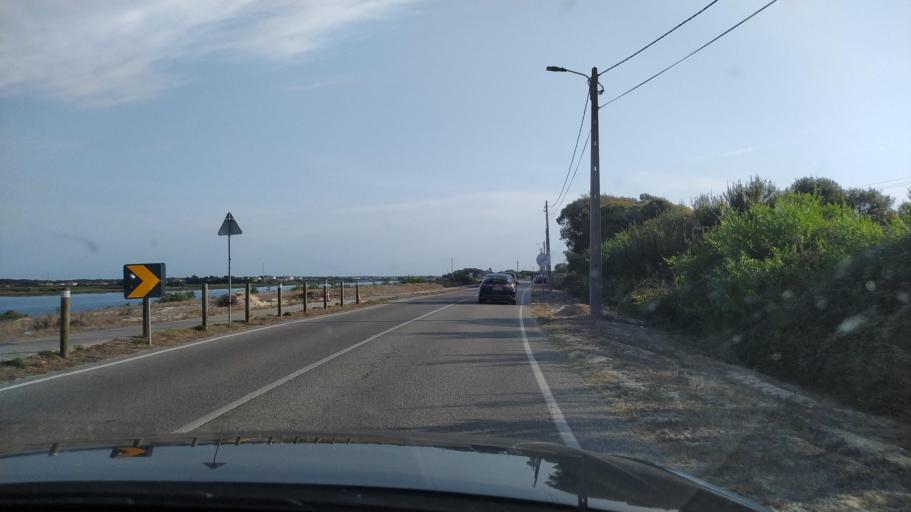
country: PT
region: Aveiro
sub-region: Ilhavo
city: Gafanha da Encarnacao
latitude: 40.5775
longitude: -8.7550
